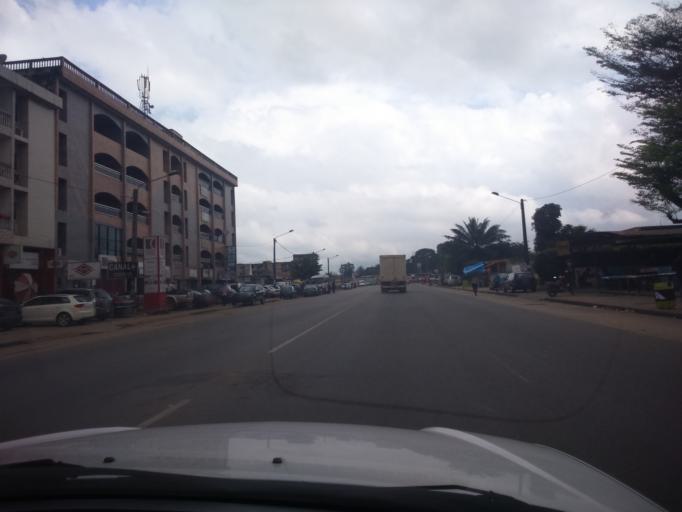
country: CI
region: Lagunes
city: Abidjan
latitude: 5.3495
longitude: -4.0633
